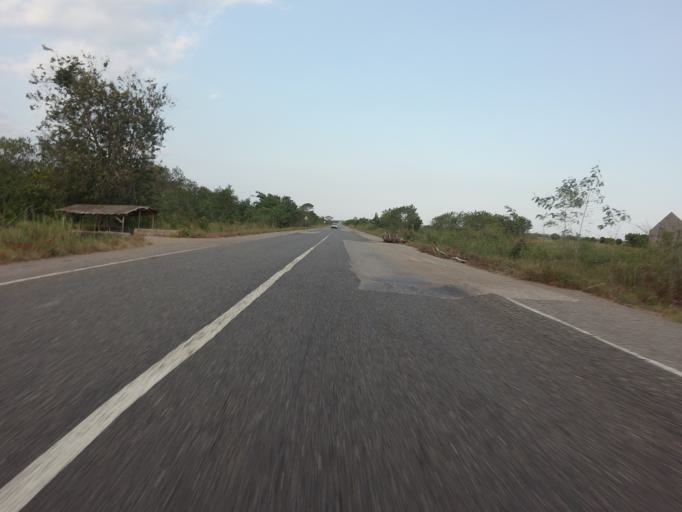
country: GH
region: Volta
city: Anloga
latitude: 6.0847
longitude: 0.5566
